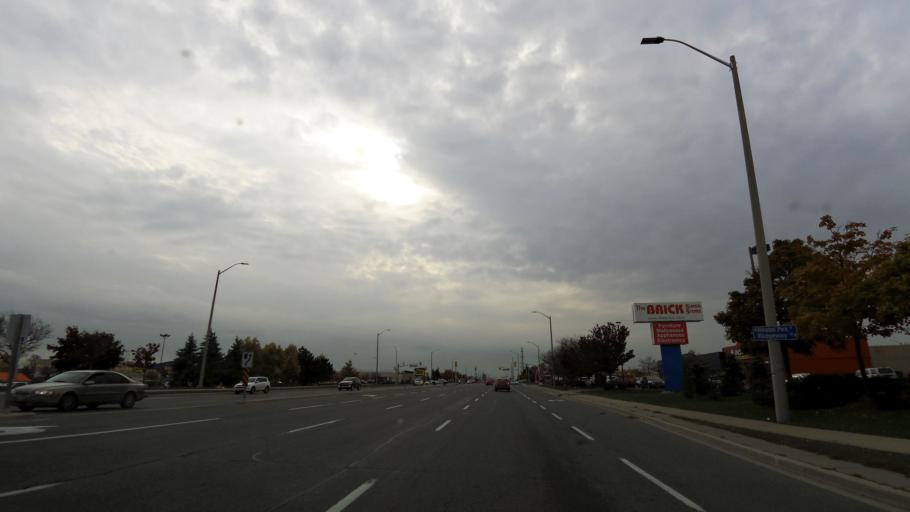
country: CA
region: Ontario
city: Mississauga
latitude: 43.5189
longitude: -79.6859
